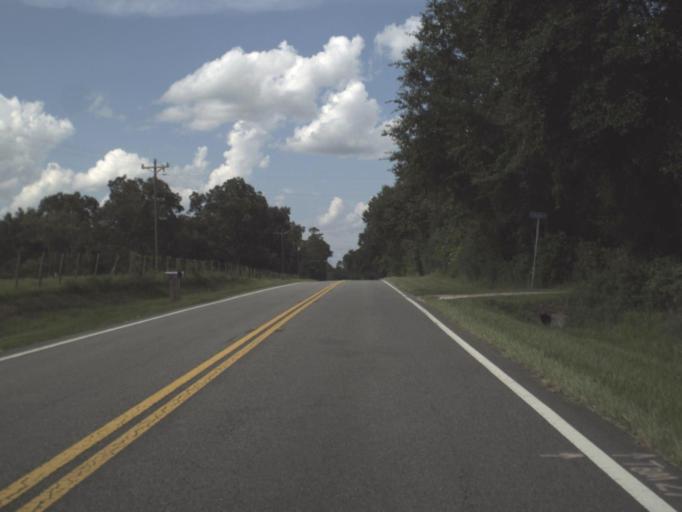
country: US
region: Florida
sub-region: Madison County
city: Madison
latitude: 30.4096
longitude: -83.6424
